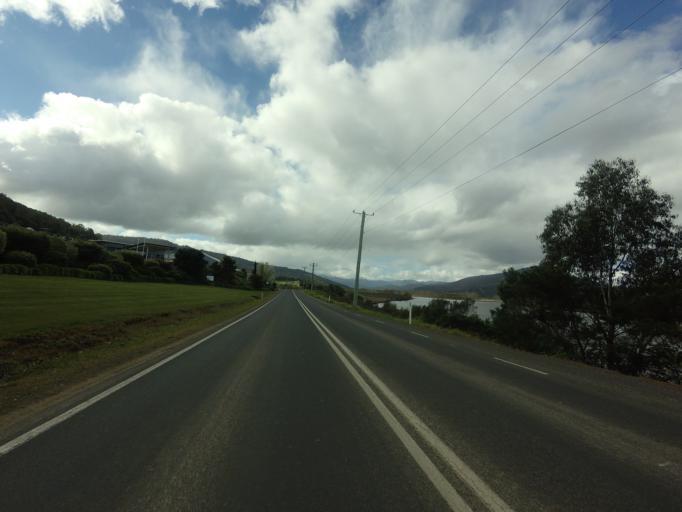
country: AU
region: Tasmania
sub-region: Huon Valley
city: Franklin
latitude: -43.0819
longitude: 147.0166
